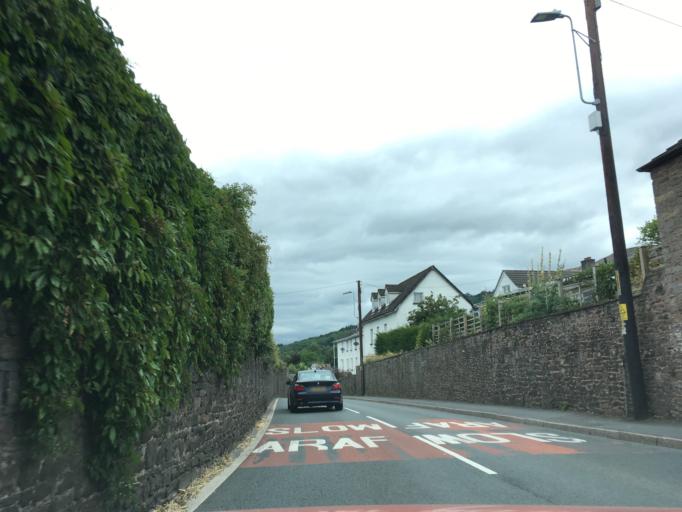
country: GB
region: Wales
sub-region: Monmouthshire
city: Gilwern
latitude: 51.8613
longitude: -3.1376
